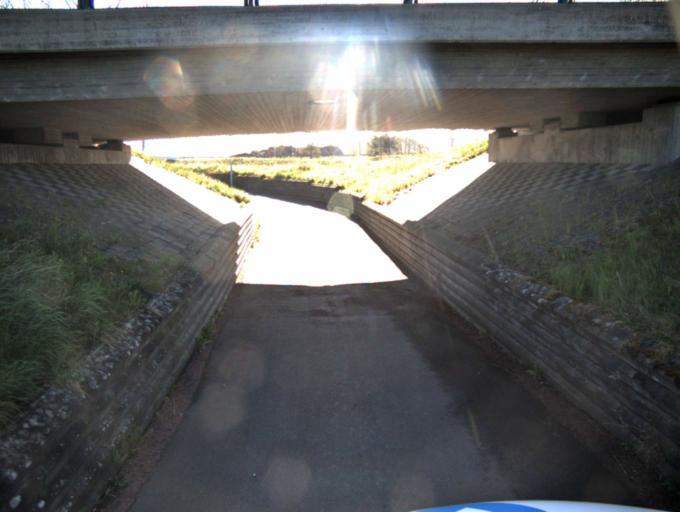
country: SE
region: Skane
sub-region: Kristianstads Kommun
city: Norra Asum
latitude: 56.0016
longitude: 14.1007
